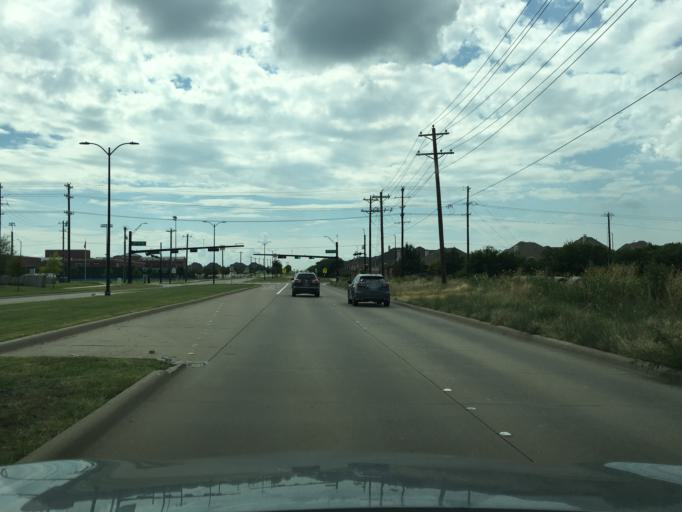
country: US
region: Texas
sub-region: Collin County
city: Frisco
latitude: 33.1331
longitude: -96.8590
